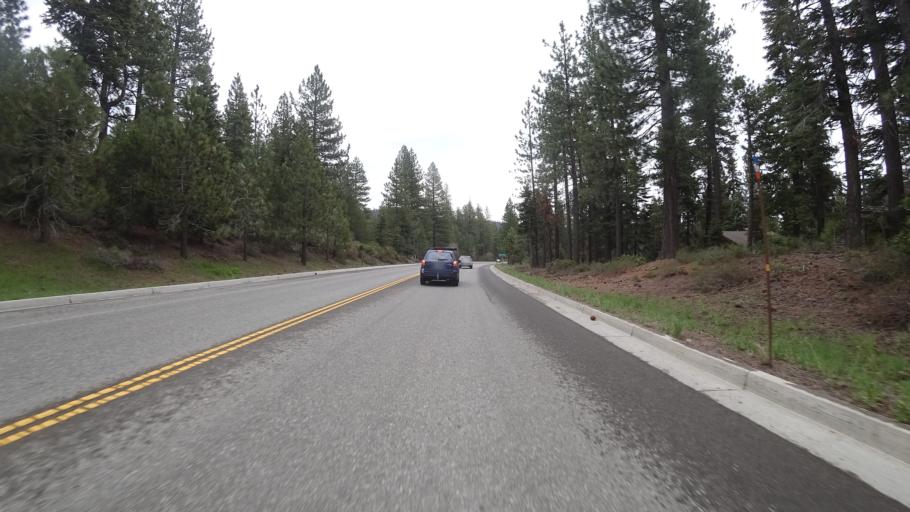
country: US
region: California
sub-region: Placer County
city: Kings Beach
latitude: 39.2524
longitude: -120.0372
